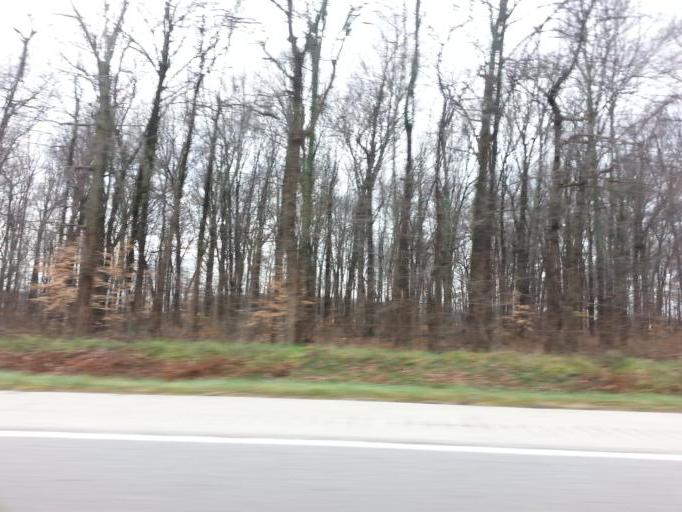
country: US
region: Indiana
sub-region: Decatur County
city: Greensburg
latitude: 39.3211
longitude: -85.3738
